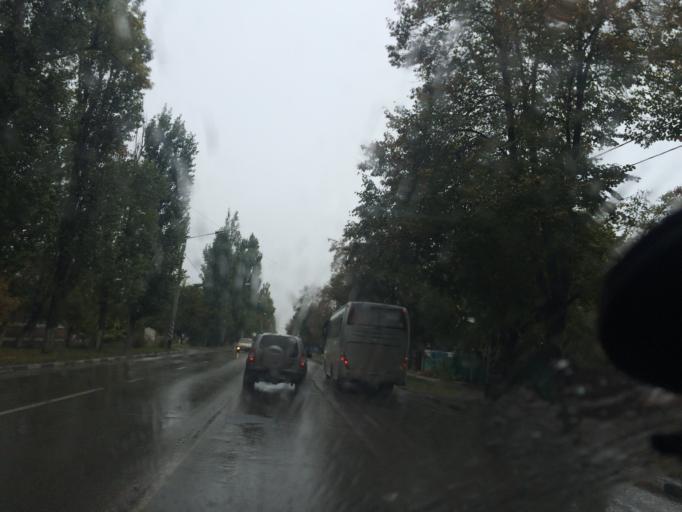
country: RU
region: Rostov
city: Azov
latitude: 47.0988
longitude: 39.4419
